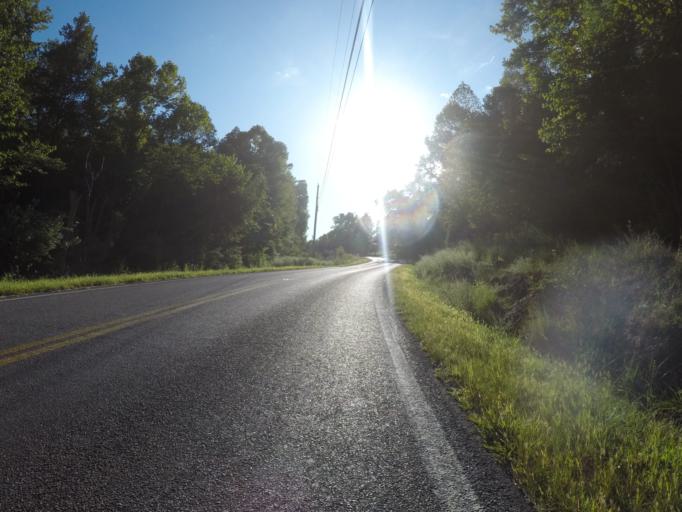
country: US
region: West Virginia
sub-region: Cabell County
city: Huntington
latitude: 38.4951
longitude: -82.4820
